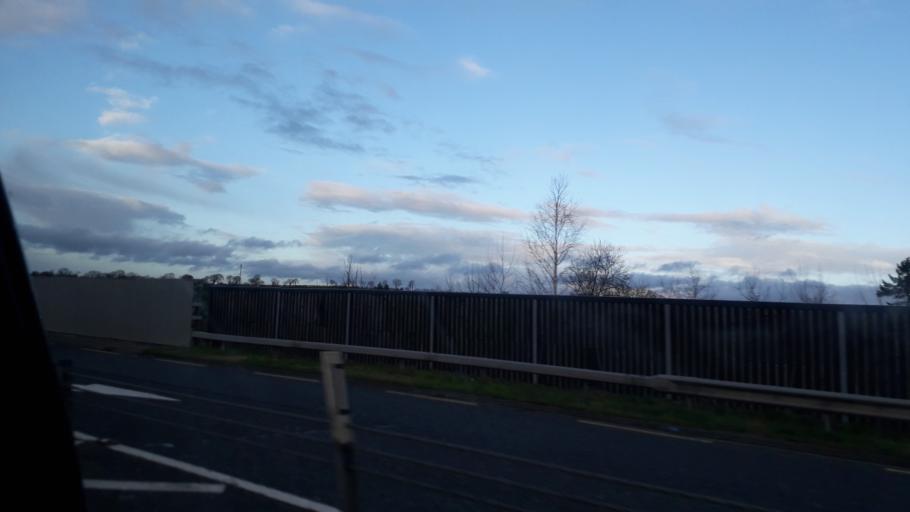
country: IE
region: Ulster
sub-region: County Monaghan
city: Castleblayney
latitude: 54.1702
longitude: -6.8100
